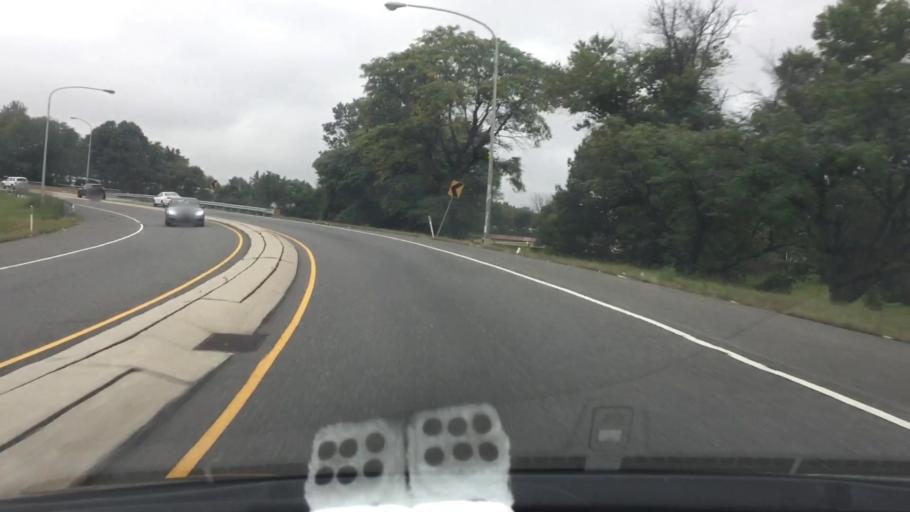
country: US
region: New Jersey
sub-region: Burlington County
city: Riverton
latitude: 40.0467
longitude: -74.9990
